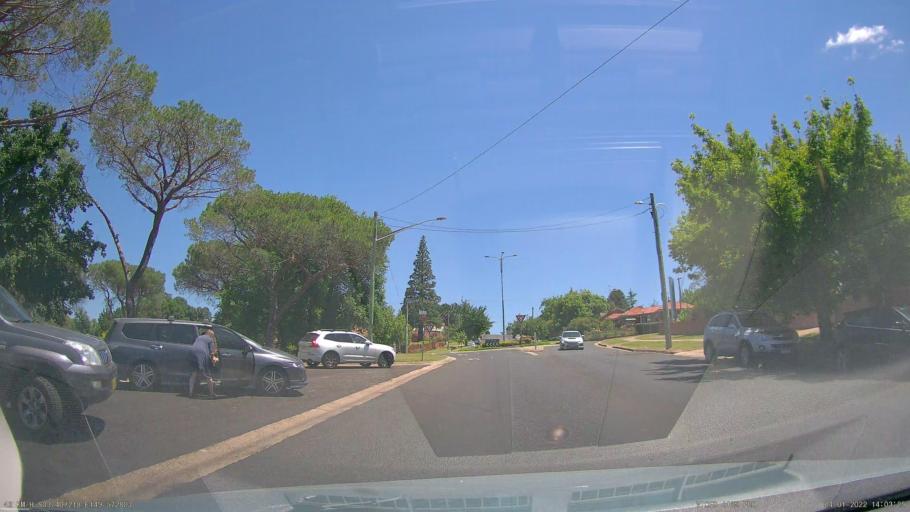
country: AU
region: New South Wales
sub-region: Bathurst Regional
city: Bathurst
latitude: -33.4073
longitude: 149.5727
